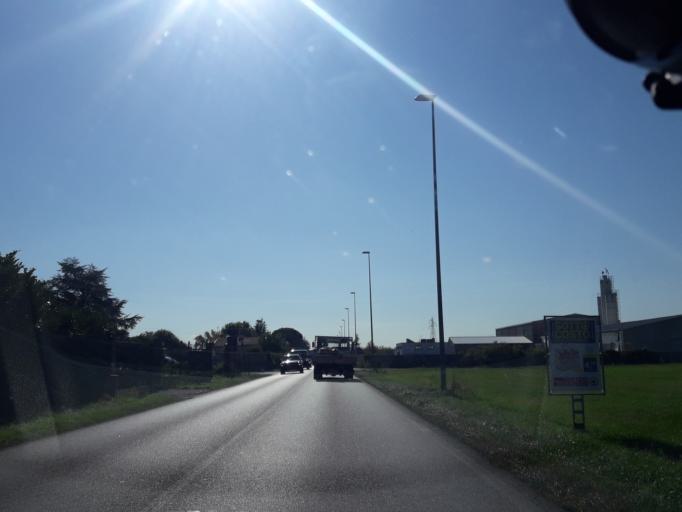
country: IT
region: Friuli Venezia Giulia
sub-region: Provincia di Udine
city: Remanzacco
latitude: 46.0822
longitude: 13.2956
